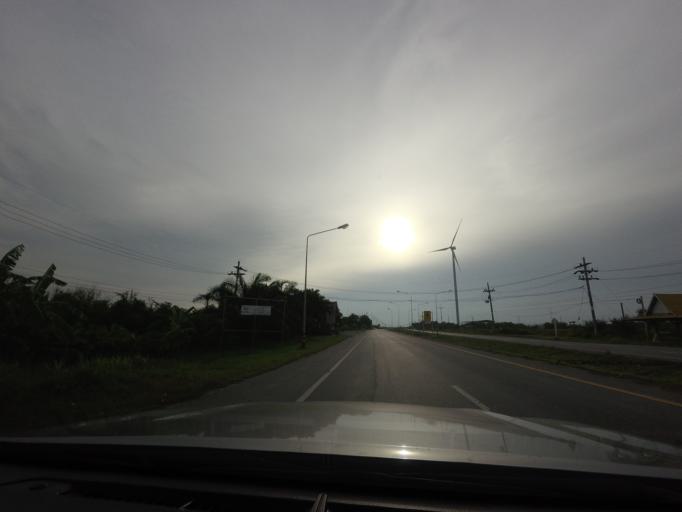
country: TH
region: Nakhon Si Thammarat
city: Hua Sai
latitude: 7.9946
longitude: 100.3219
